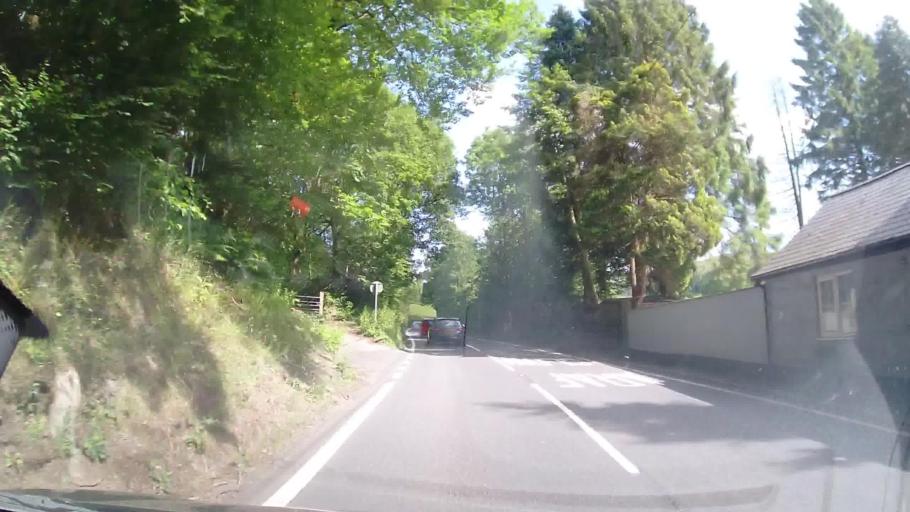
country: GB
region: Wales
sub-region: Gwynedd
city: Corris
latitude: 52.7026
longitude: -3.6633
